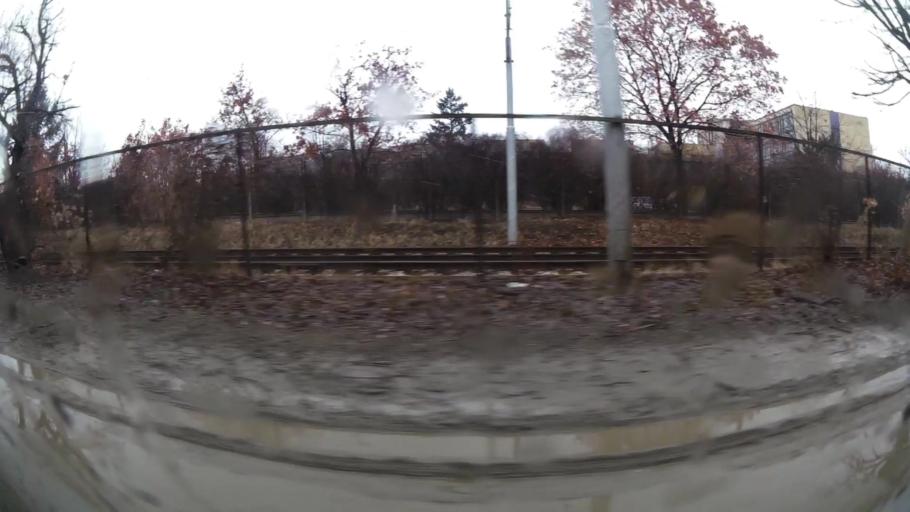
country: BG
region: Sofia-Capital
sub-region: Stolichna Obshtina
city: Sofia
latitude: 42.6611
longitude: 23.4154
